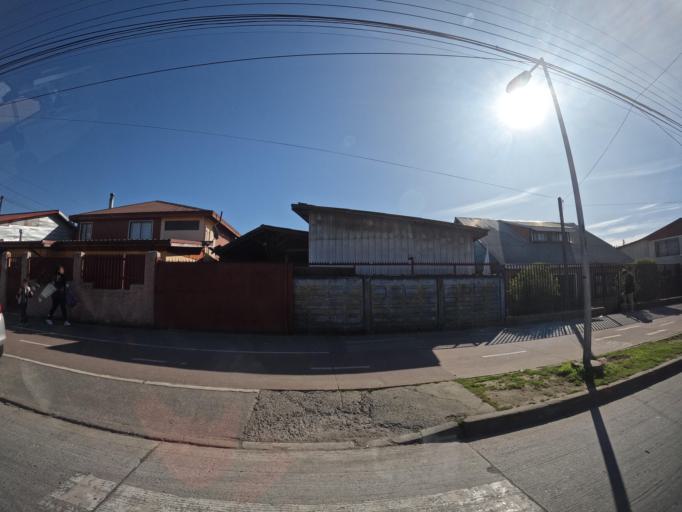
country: CL
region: Biobio
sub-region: Provincia de Concepcion
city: Chiguayante
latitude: -36.9720
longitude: -72.9365
